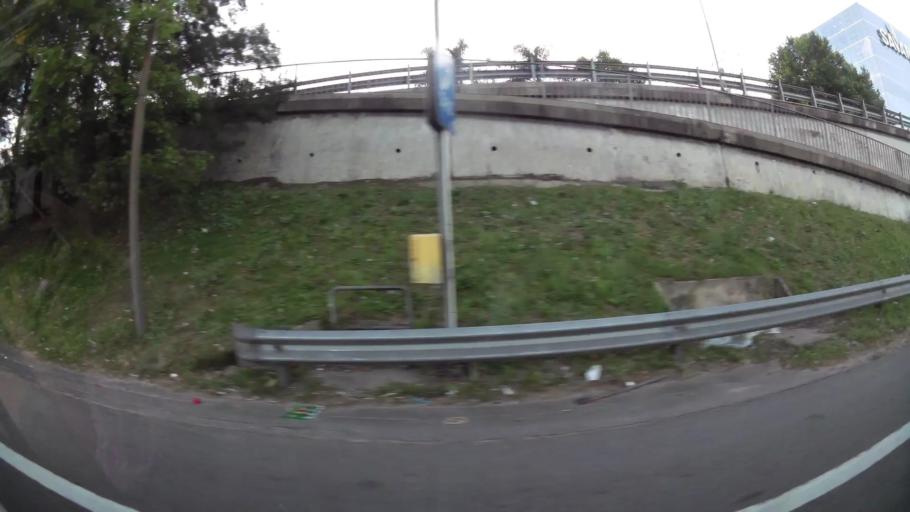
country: AR
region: Buenos Aires
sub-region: Partido de Vicente Lopez
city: Olivos
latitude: -34.5384
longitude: -58.5009
